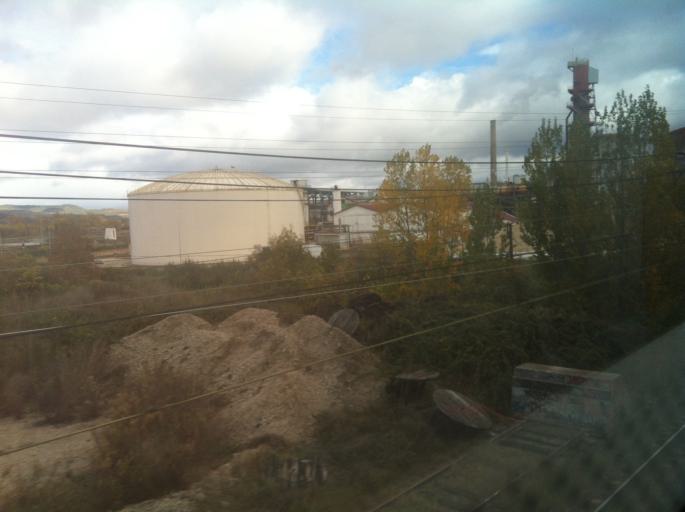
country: ES
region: Castille and Leon
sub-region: Provincia de Burgos
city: Miranda de Ebro
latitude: 42.6950
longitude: -2.9291
